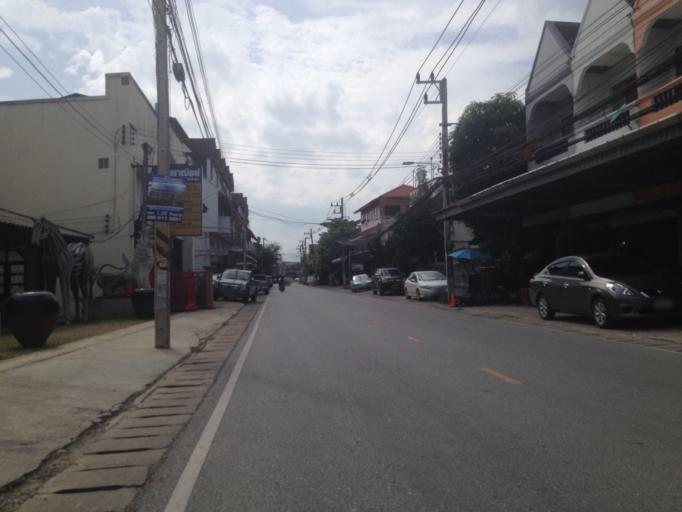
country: TH
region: Chiang Mai
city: Hang Dong
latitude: 18.6880
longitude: 98.9228
